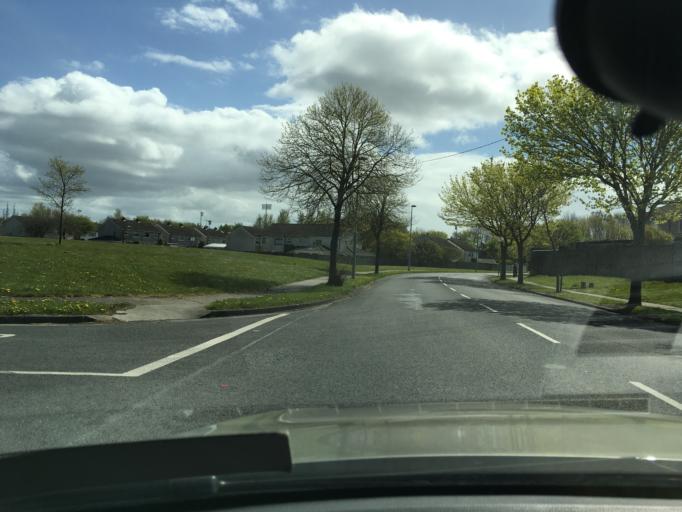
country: IE
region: Leinster
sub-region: Fingal County
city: Blanchardstown
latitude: 53.3994
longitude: -6.3732
